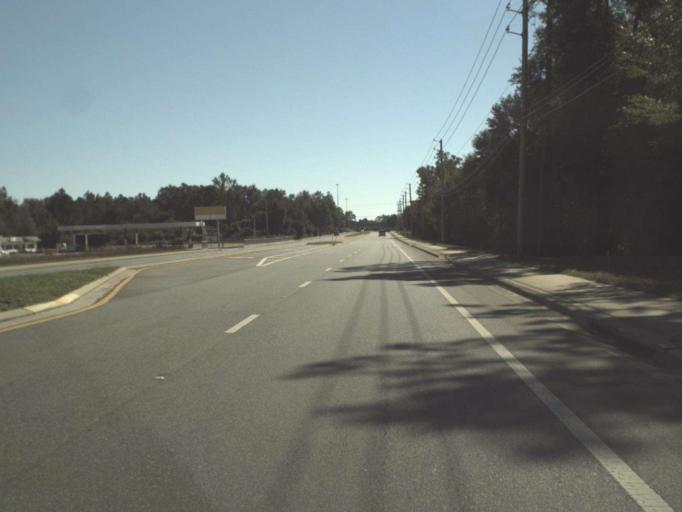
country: US
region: Florida
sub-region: Santa Rosa County
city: East Milton
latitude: 30.6260
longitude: -86.9672
